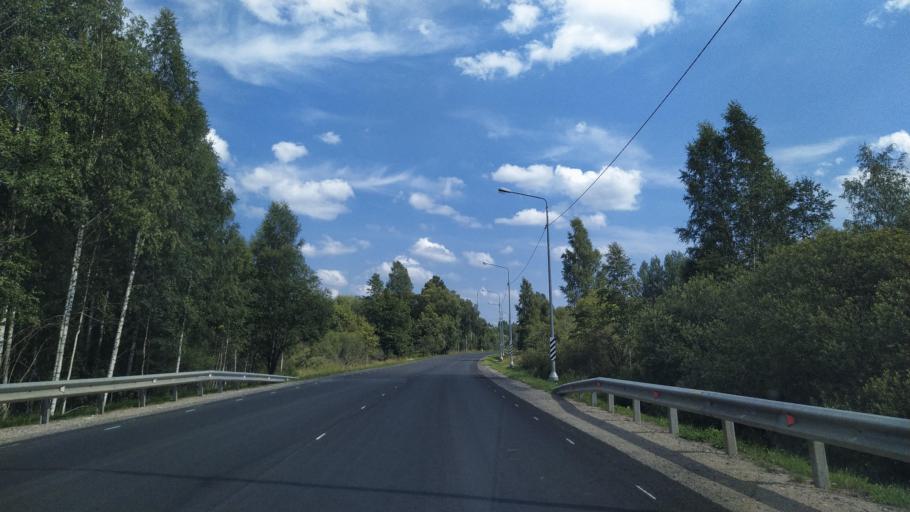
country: RU
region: Pskov
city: Porkhov
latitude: 57.7272
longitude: 29.1649
